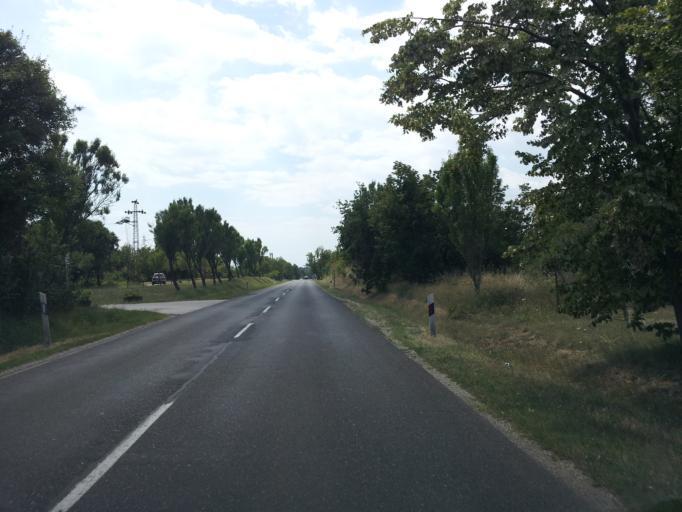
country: HU
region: Somogy
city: Balatonszarszo
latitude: 46.9003
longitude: 17.7924
